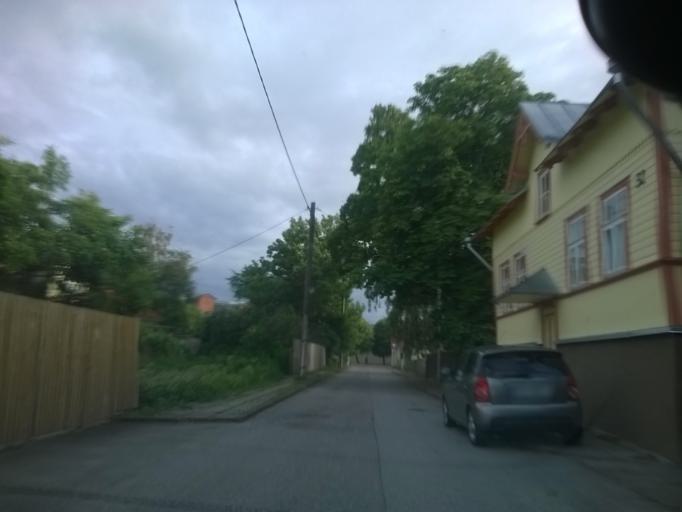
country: EE
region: Laeaene
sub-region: Haapsalu linn
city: Haapsalu
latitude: 58.9402
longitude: 23.5354
